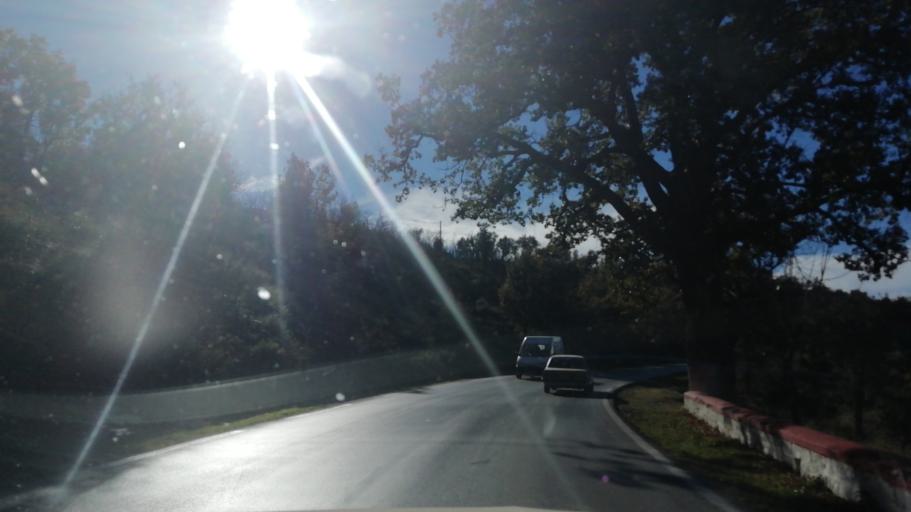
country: DZ
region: Tlemcen
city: Mansoura
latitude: 34.8392
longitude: -1.3686
